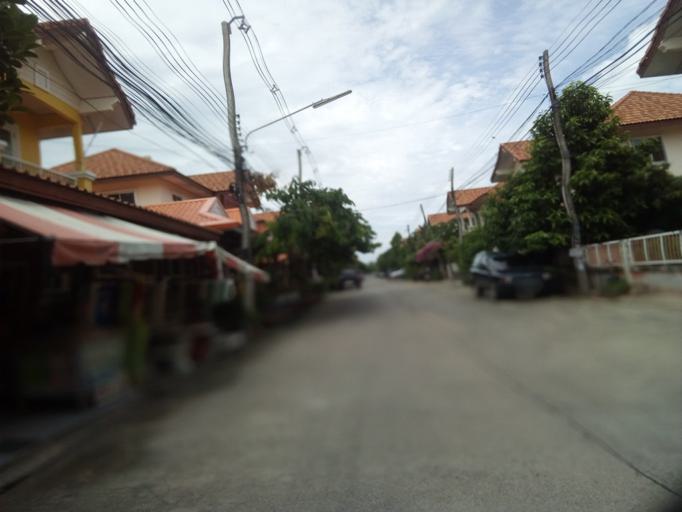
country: TH
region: Pathum Thani
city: Ban Rangsit
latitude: 14.0515
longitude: 100.8350
